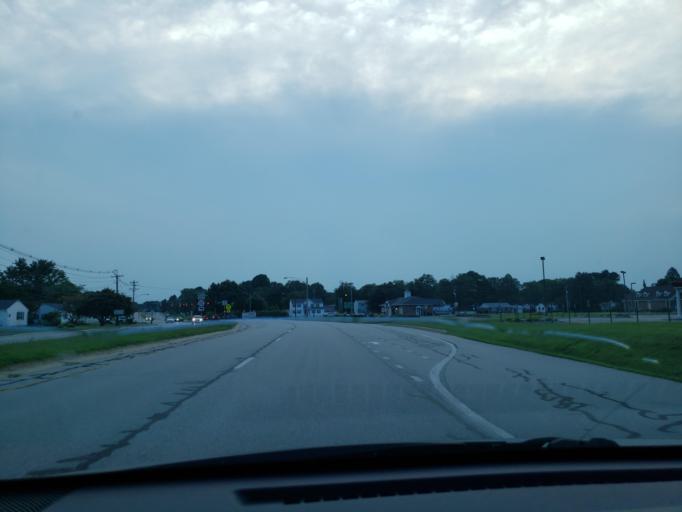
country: US
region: Delaware
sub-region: Kent County
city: Highland Acres
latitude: 39.1184
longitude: -75.5133
